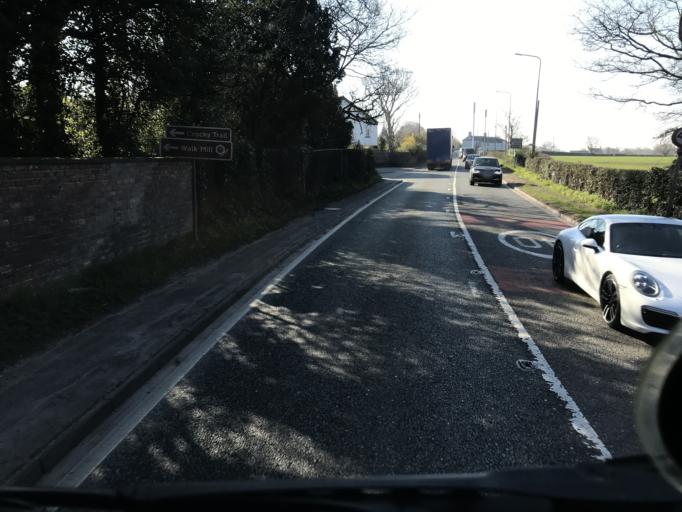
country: GB
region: England
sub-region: Cheshire West and Chester
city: Waverton
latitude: 53.1708
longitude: -2.8215
